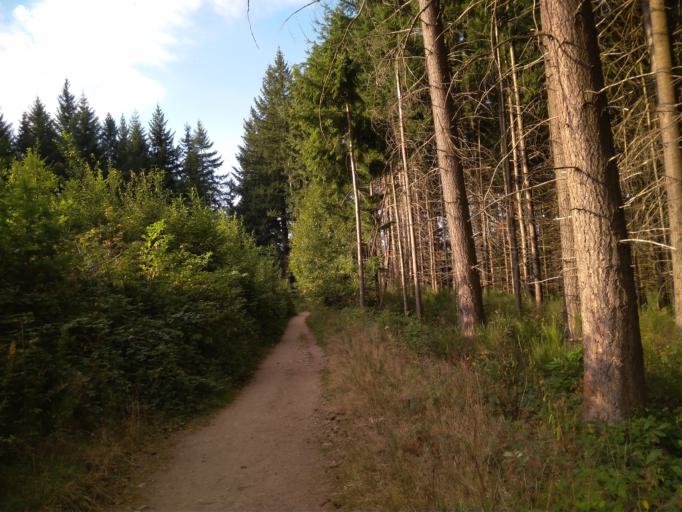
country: FR
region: Auvergne
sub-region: Departement de l'Allier
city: Le Mayet-de-Montagne
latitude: 46.1280
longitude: 3.7627
